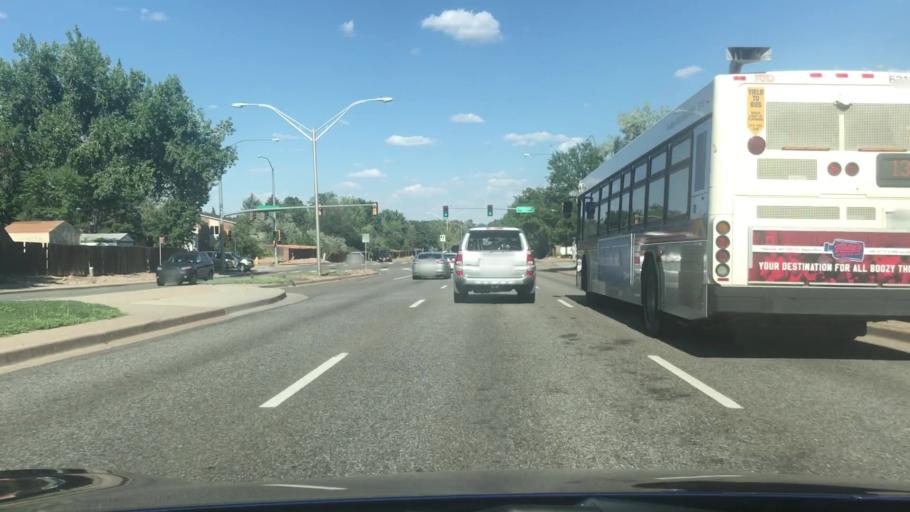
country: US
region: Colorado
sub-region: Arapahoe County
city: Dove Valley
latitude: 39.6530
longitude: -104.8041
